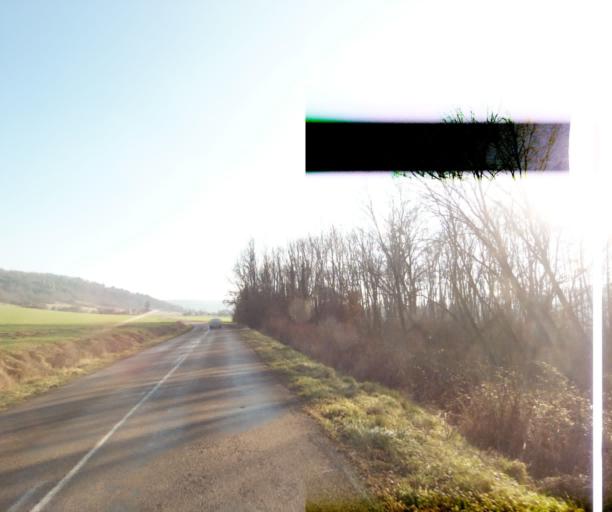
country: FR
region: Champagne-Ardenne
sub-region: Departement de la Haute-Marne
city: Chevillon
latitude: 48.5010
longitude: 5.1289
